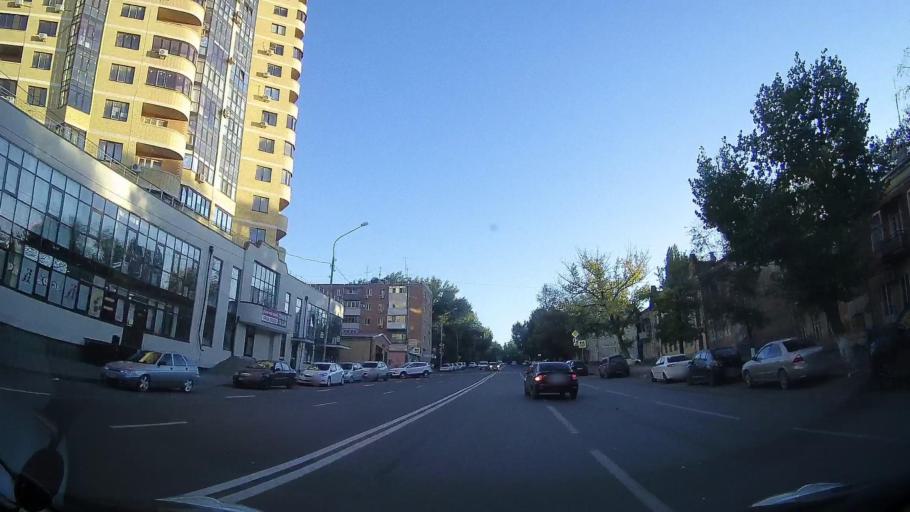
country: RU
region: Rostov
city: Rostov-na-Donu
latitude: 47.2428
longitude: 39.7016
